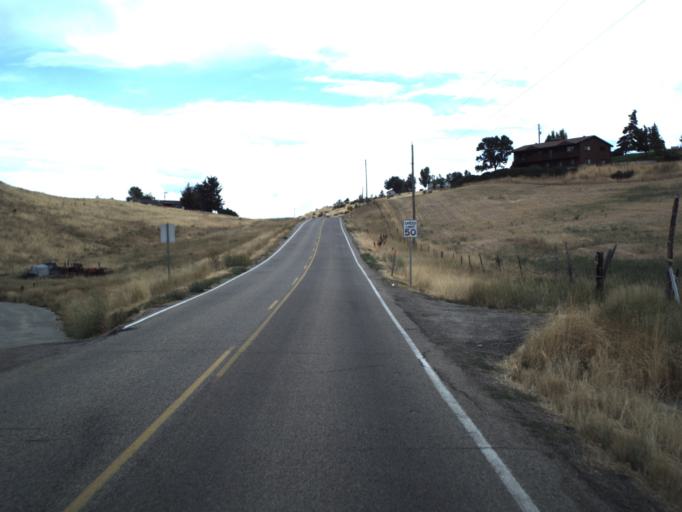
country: US
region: Utah
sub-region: Morgan County
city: Morgan
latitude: 40.9888
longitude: -111.6793
